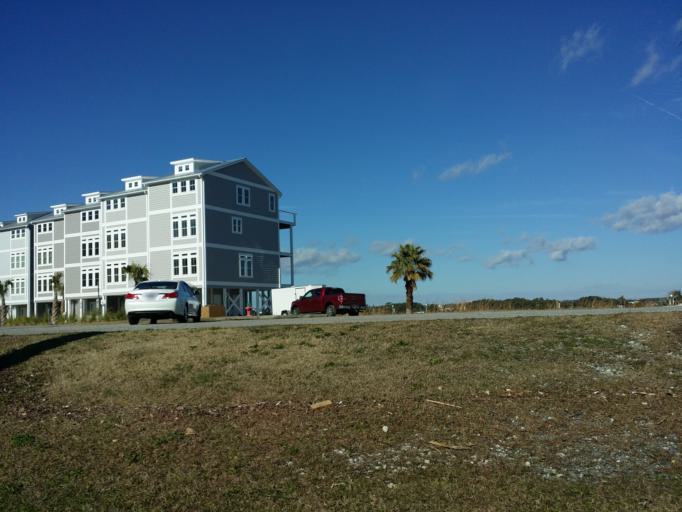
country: US
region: North Carolina
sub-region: Pender County
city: Surf City
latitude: 34.4285
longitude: -77.5435
